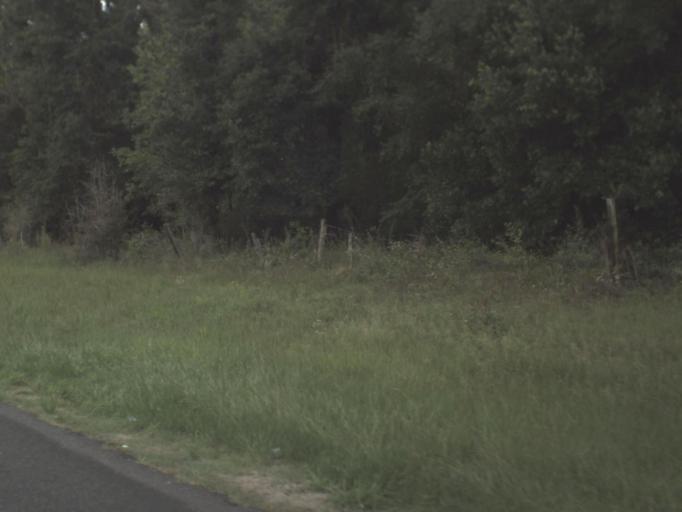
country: US
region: Florida
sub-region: Levy County
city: Williston
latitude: 29.2971
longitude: -82.4480
